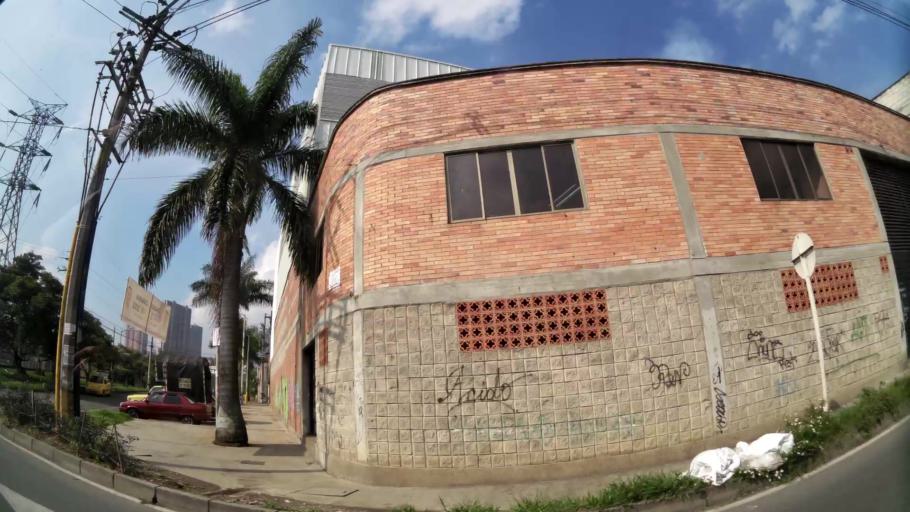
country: CO
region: Antioquia
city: La Estrella
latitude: 6.1731
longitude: -75.6314
